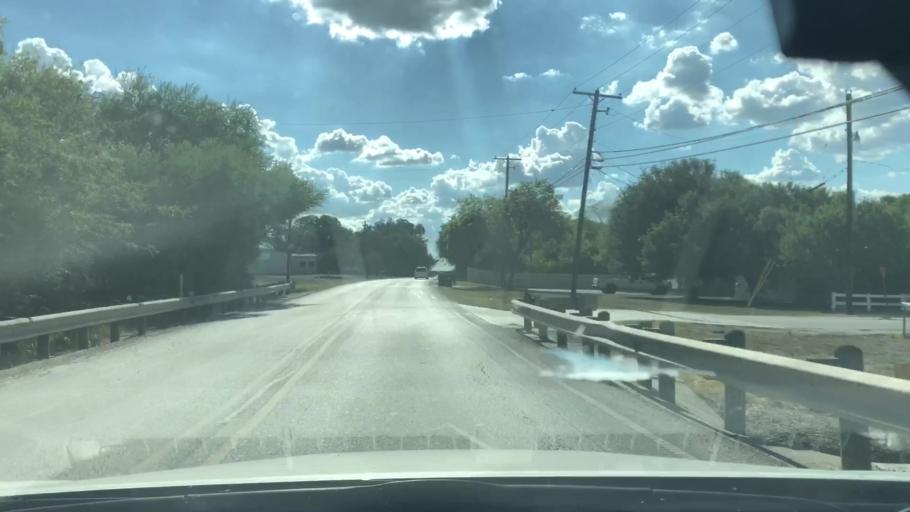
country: US
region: Texas
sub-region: Guadalupe County
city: Northcliff
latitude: 29.6624
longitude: -98.1839
